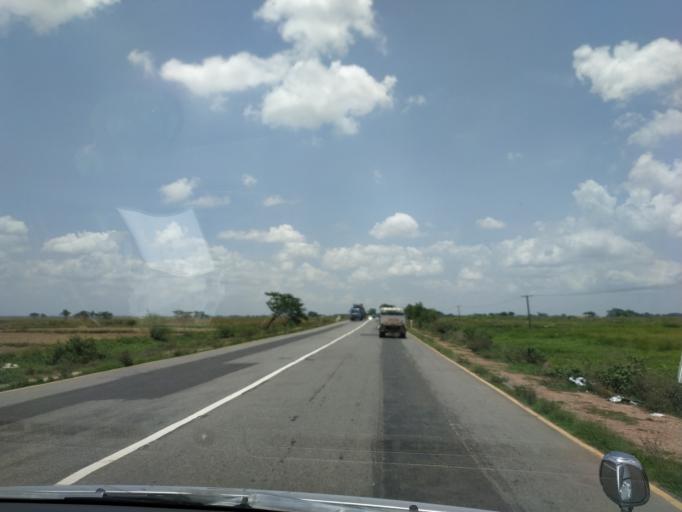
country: MM
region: Bago
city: Bago
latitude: 17.4635
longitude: 96.5911
